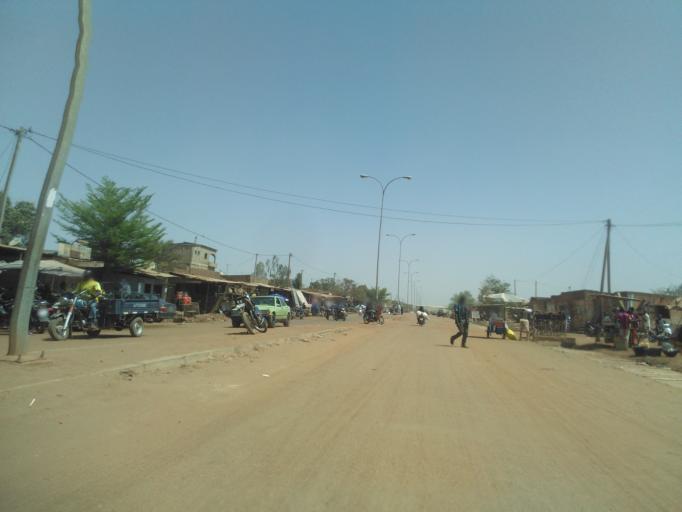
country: BF
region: Centre
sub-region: Kadiogo Province
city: Ouagadougou
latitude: 12.3892
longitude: -1.5635
